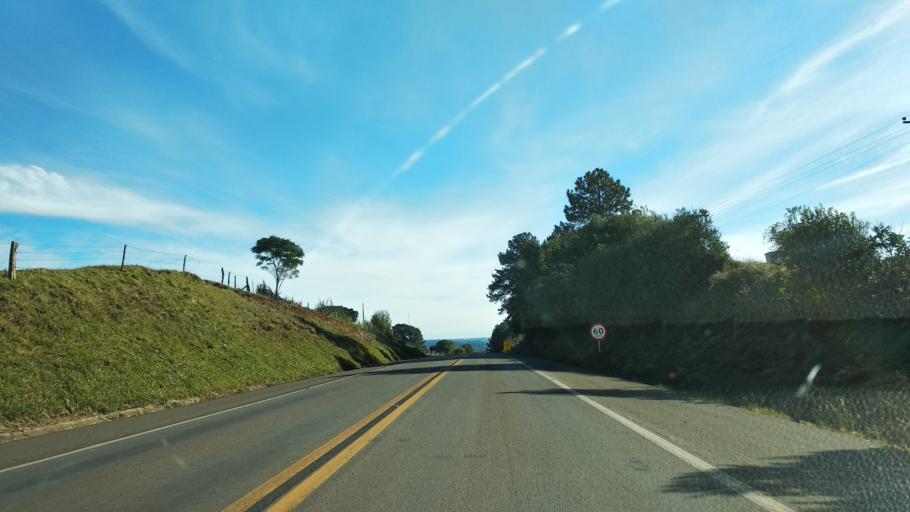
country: BR
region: Santa Catarina
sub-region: Celso Ramos
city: Celso Ramos
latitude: -27.5285
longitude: -51.3828
